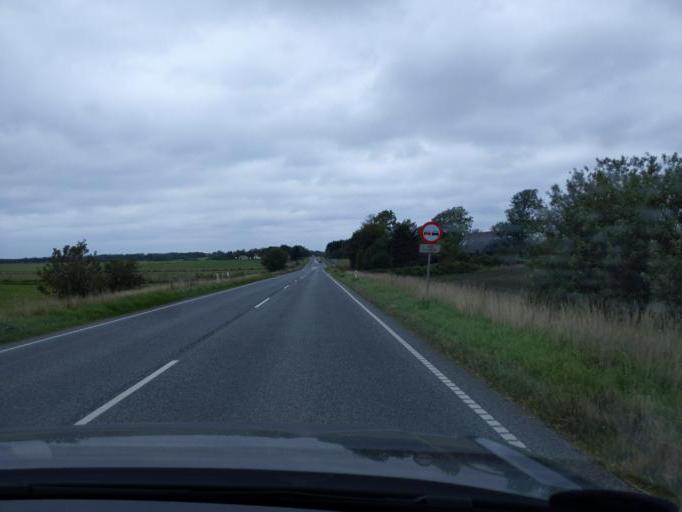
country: DK
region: North Denmark
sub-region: Mariagerfjord Kommune
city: Mariager
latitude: 56.5378
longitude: 9.8993
